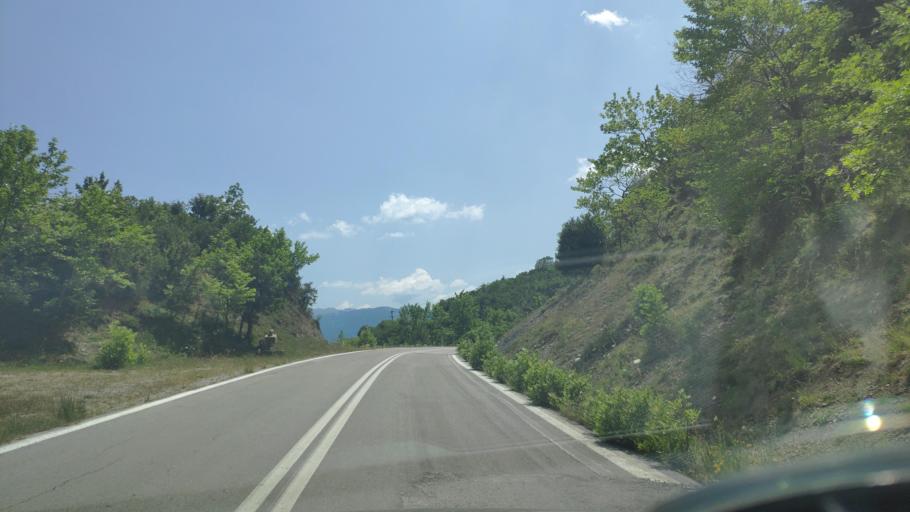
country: GR
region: Thessaly
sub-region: Nomos Kardhitsas
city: Anthiro
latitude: 39.2684
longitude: 21.3501
